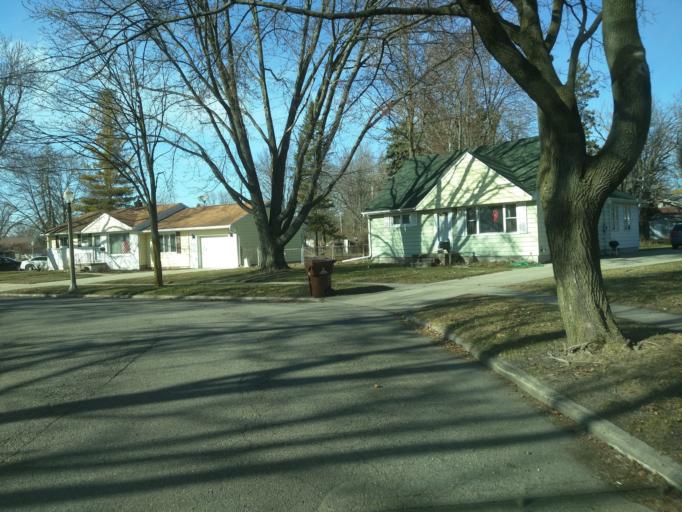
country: US
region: Michigan
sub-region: Ingham County
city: Edgemont Park
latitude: 42.7645
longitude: -84.5973
